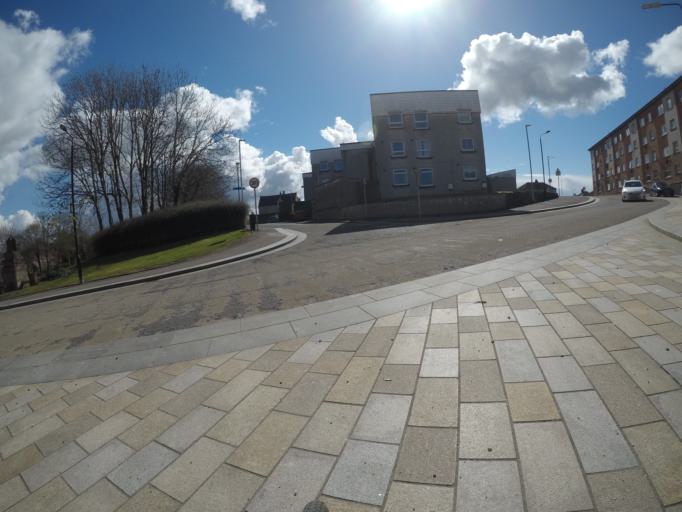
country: GB
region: Scotland
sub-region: North Ayrshire
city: Kilwinning
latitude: 55.6539
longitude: -4.6961
